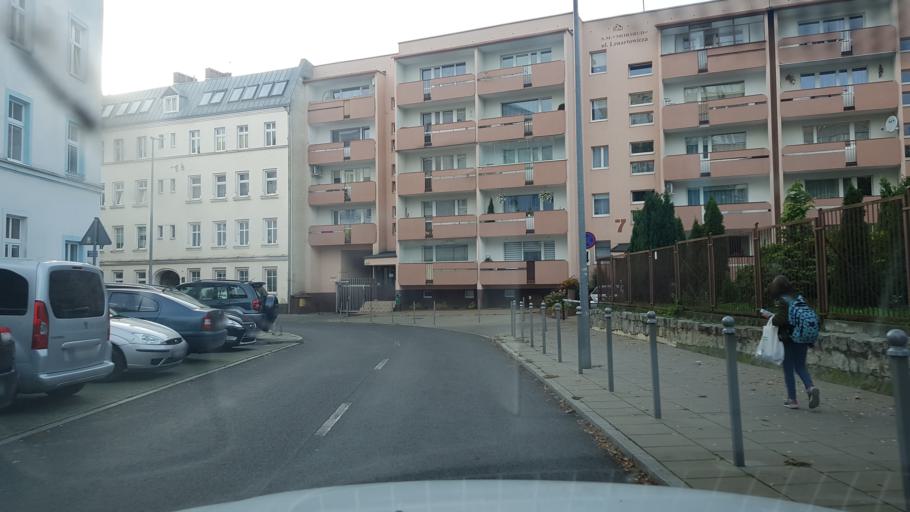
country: PL
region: West Pomeranian Voivodeship
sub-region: Szczecin
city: Szczecin
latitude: 53.4482
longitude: 14.5428
